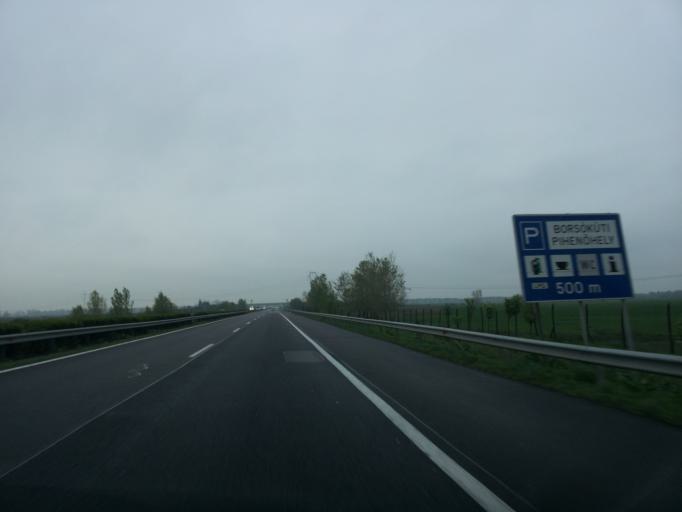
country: HU
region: Heves
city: Adacs
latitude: 47.7200
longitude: 19.9927
